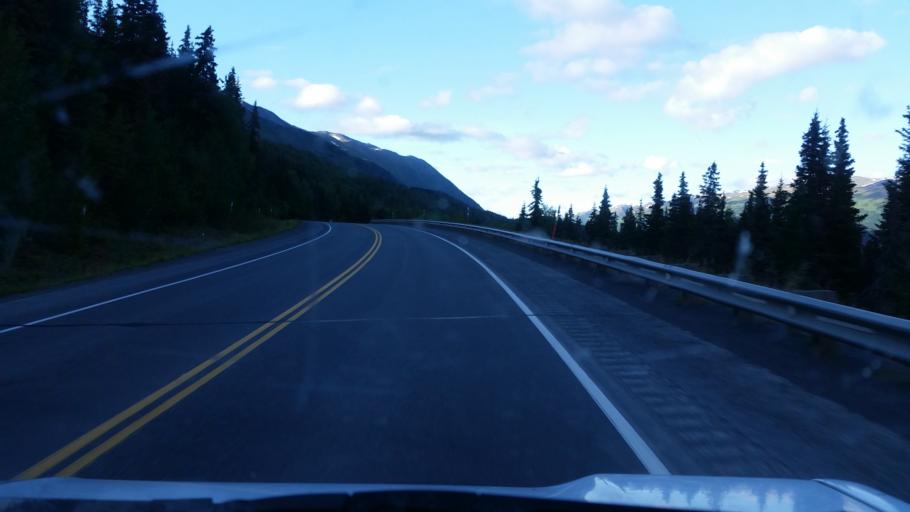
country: US
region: Alaska
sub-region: Kenai Peninsula Borough
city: Bear Creek
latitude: 60.5082
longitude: -149.6852
